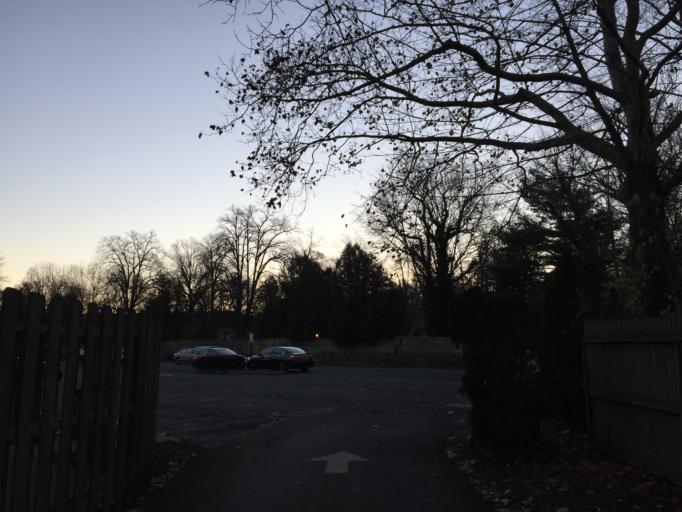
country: US
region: New Jersey
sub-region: Union County
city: Summit
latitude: 40.7145
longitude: -74.3665
